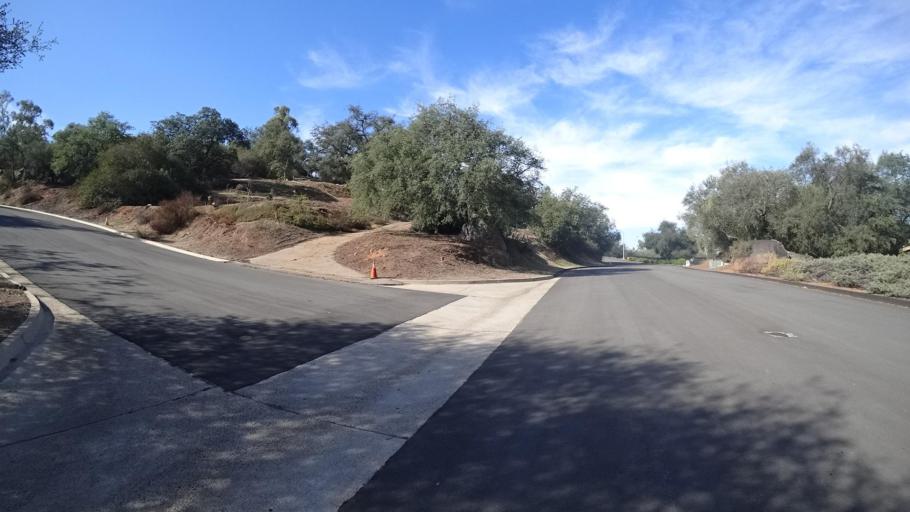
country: US
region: California
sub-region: San Diego County
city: Alpine
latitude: 32.8149
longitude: -116.7726
